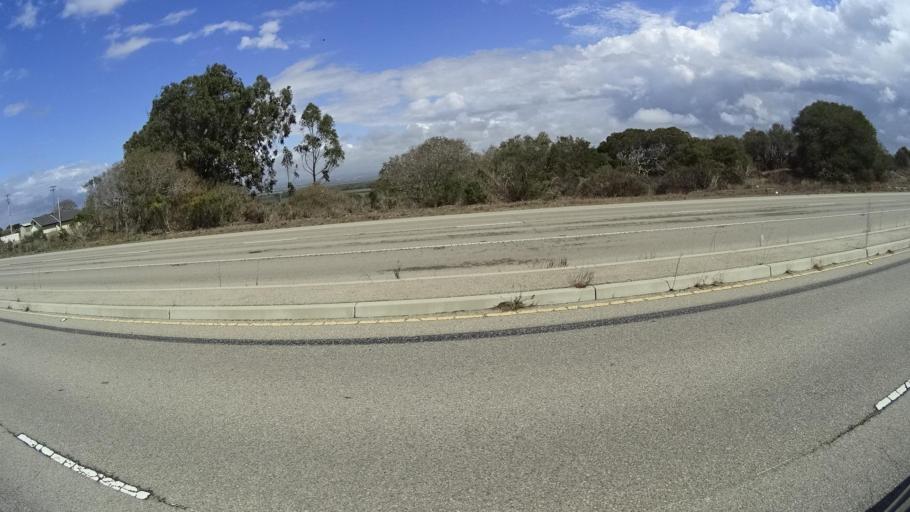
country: US
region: California
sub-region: Monterey County
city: Marina
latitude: 36.6588
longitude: -121.7407
